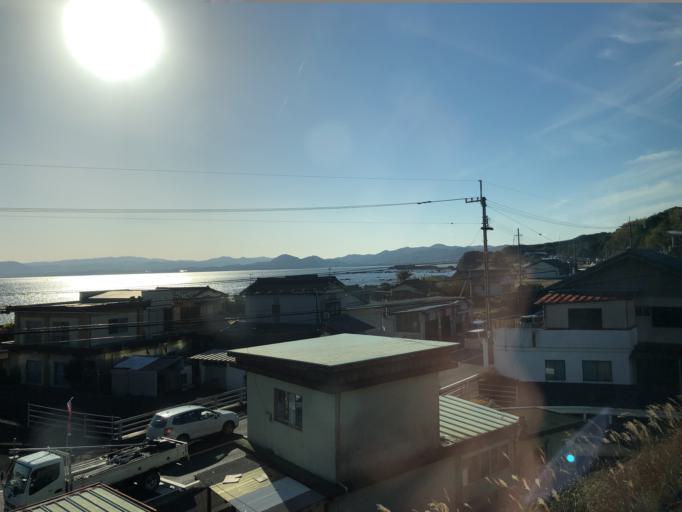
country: JP
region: Kochi
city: Nakamura
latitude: 33.0380
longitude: 133.0727
